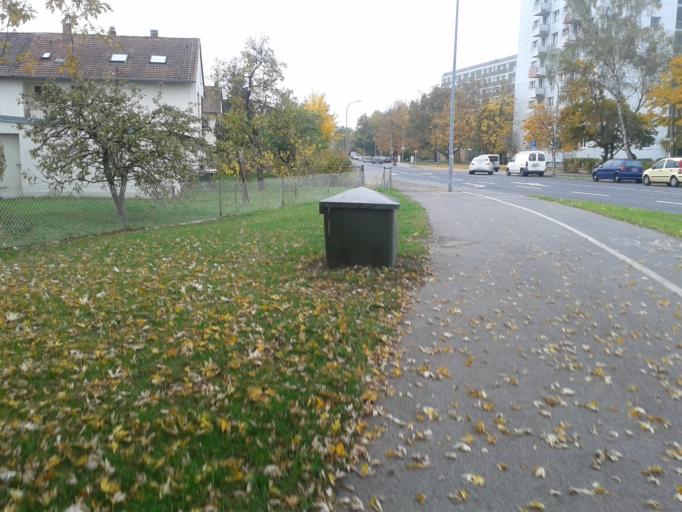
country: DE
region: Bavaria
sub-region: Upper Franconia
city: Bamberg
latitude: 49.9107
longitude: 10.9107
